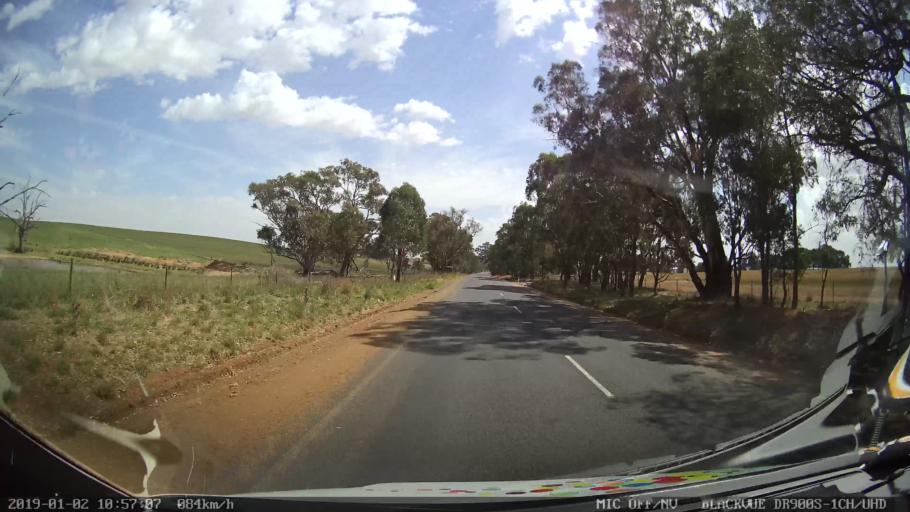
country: AU
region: New South Wales
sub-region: Cootamundra
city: Cootamundra
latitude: -34.6392
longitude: 148.2808
